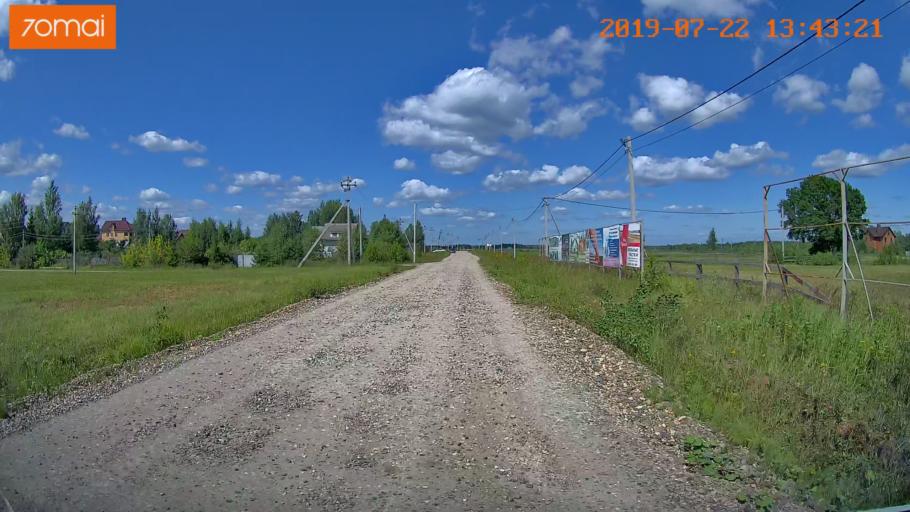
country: RU
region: Ivanovo
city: Novo-Talitsy
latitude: 57.0826
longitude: 40.8743
